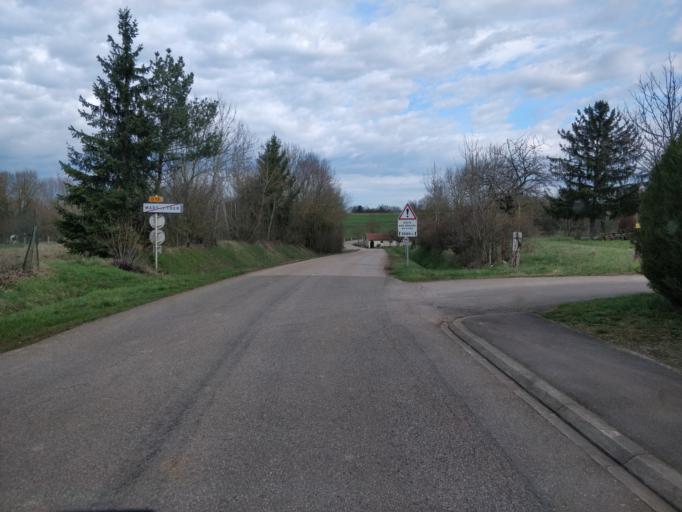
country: FR
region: Lorraine
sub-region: Departement de Meurthe-et-Moselle
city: Jarny
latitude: 49.1011
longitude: 5.8893
